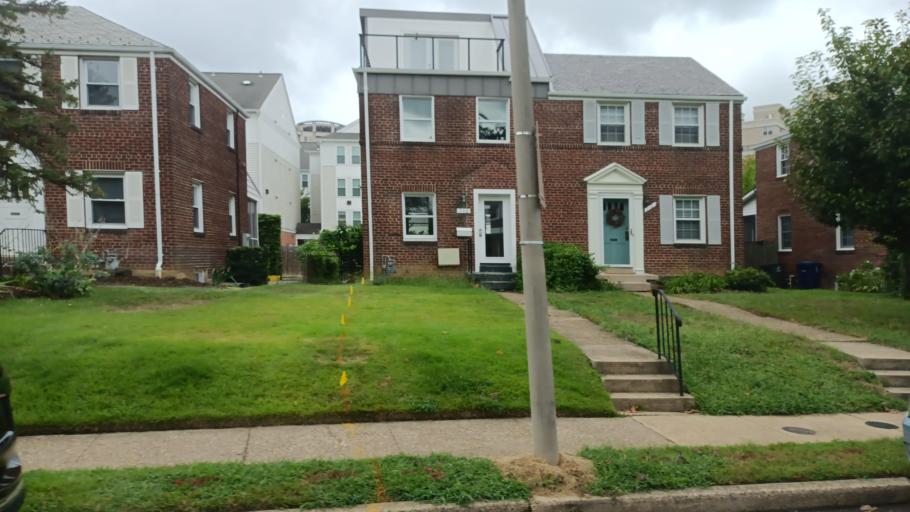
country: US
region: Virginia
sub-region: Arlington County
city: Arlington
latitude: 38.8801
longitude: -77.1040
